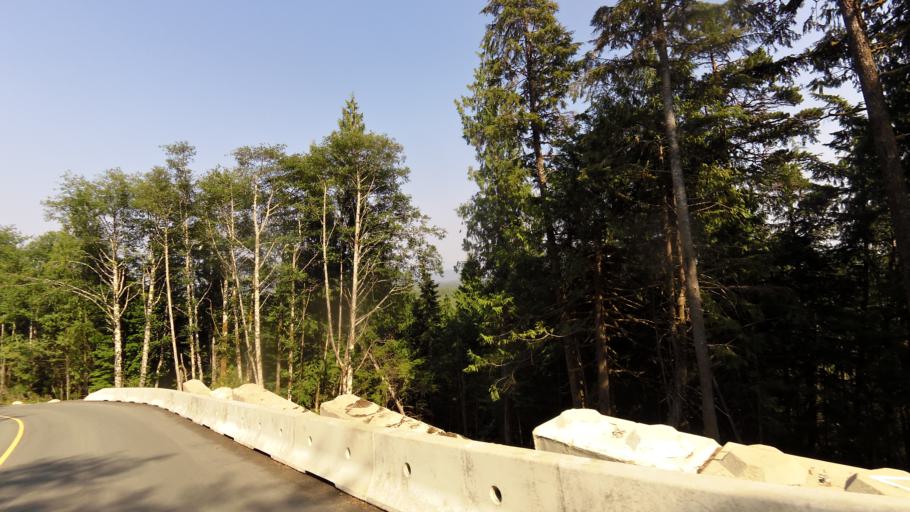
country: CA
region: British Columbia
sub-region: Regional District of Alberni-Clayoquot
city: Tofino
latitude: 49.0841
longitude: -125.8395
